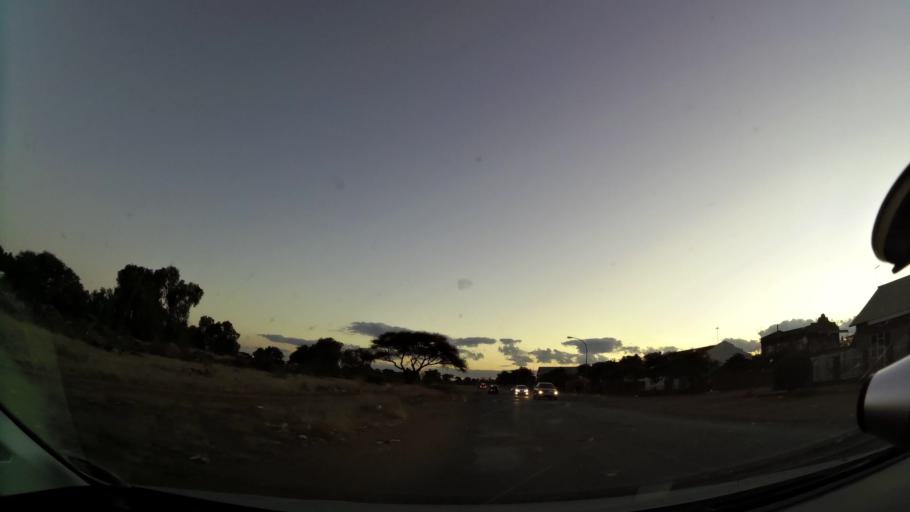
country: ZA
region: Northern Cape
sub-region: Frances Baard District Municipality
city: Kimberley
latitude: -28.7233
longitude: 24.7655
